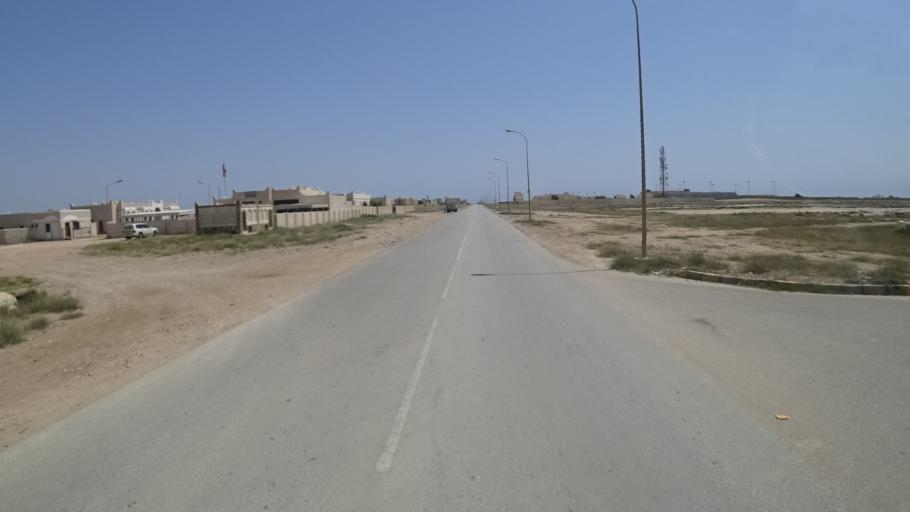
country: OM
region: Zufar
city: Salalah
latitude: 16.9869
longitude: 54.6979
